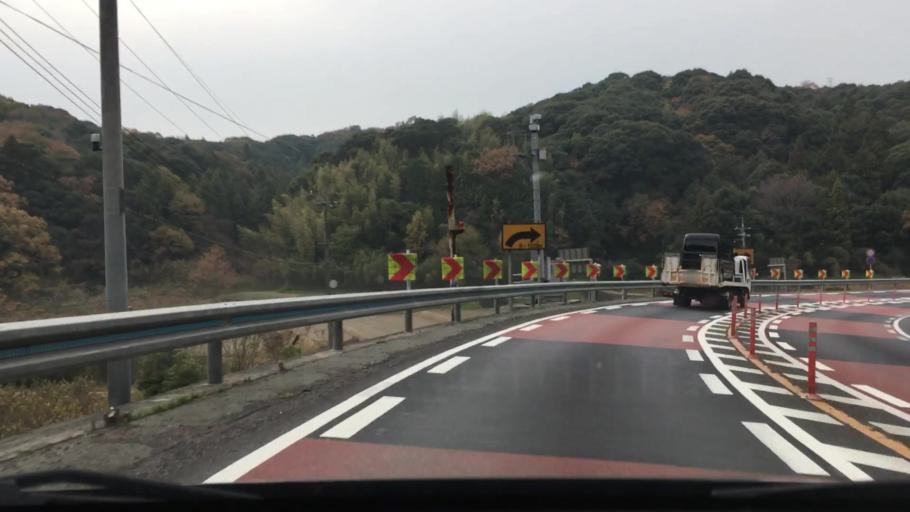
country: JP
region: Yamaguchi
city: Onoda
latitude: 34.0364
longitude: 131.2529
